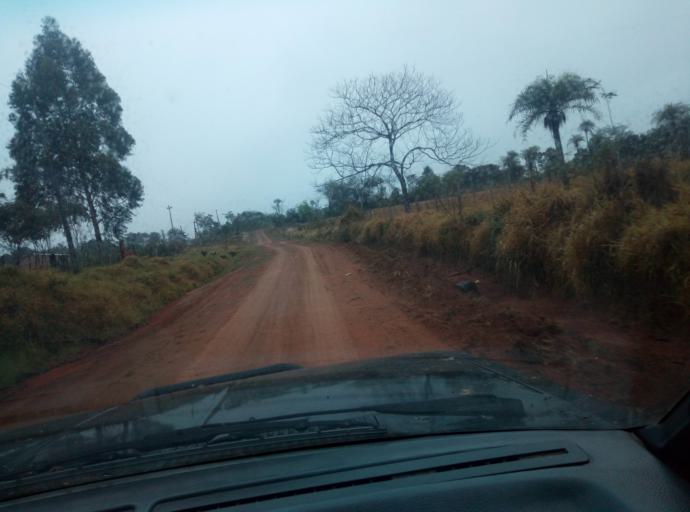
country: PY
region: Caaguazu
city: Carayao
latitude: -25.1904
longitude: -56.3171
